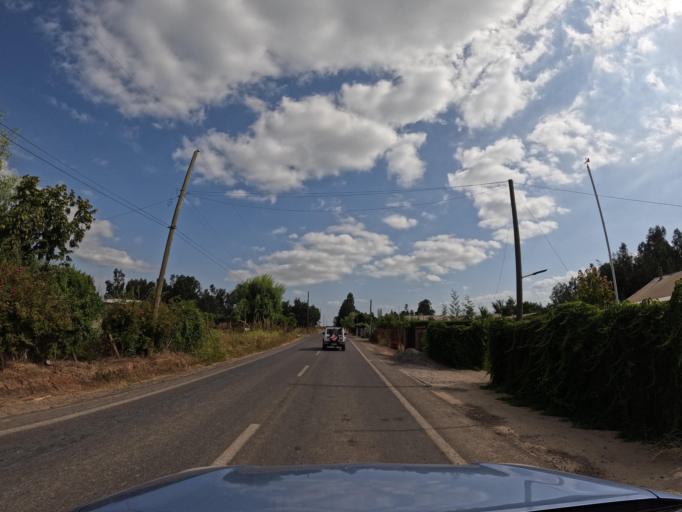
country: CL
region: Maule
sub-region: Provincia de Curico
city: Molina
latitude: -35.1990
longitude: -71.2973
